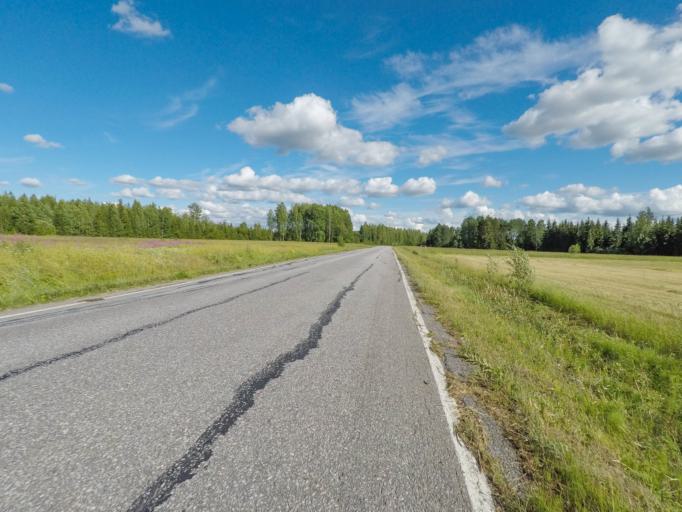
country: FI
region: South Karelia
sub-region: Imatra
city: Imatra
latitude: 61.1358
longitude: 28.6557
